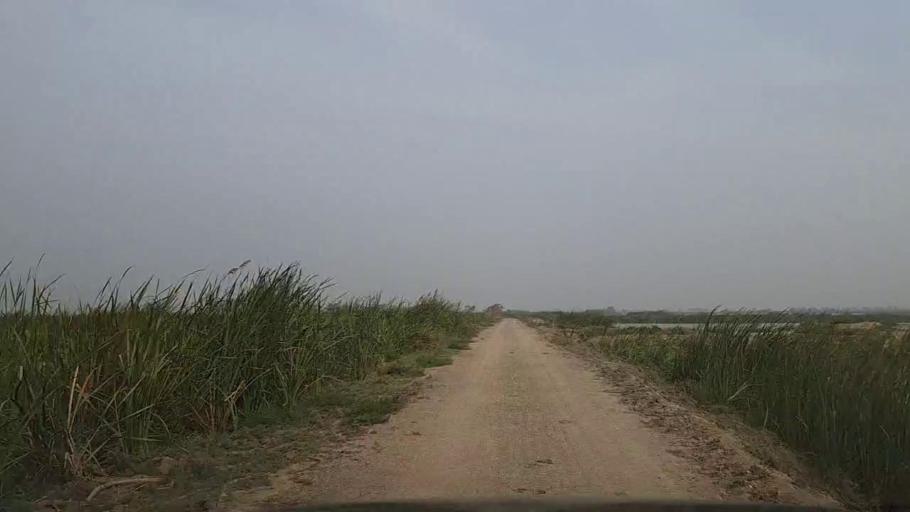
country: PK
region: Sindh
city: Chuhar Jamali
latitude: 24.5049
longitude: 67.8907
